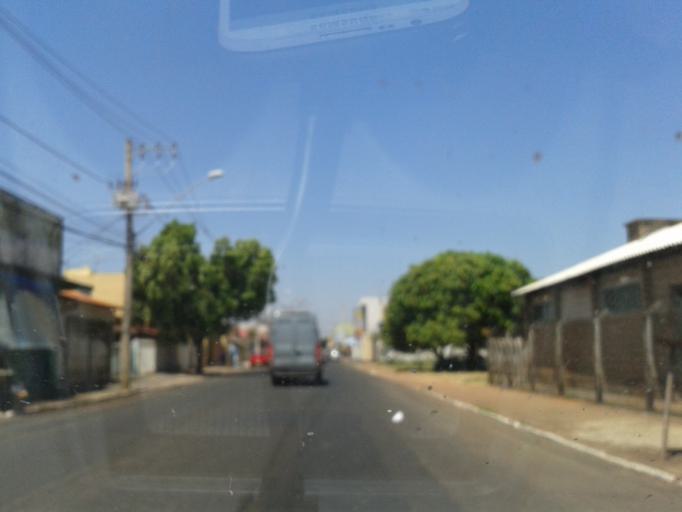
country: BR
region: Minas Gerais
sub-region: Araguari
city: Araguari
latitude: -18.6620
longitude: -48.1847
